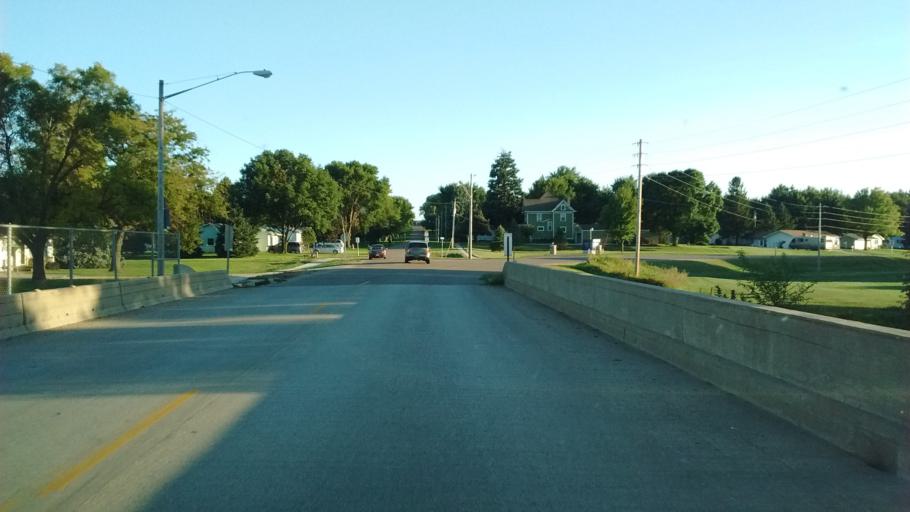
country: US
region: Iowa
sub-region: Plymouth County
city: Kingsley
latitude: 42.5856
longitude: -95.9674
